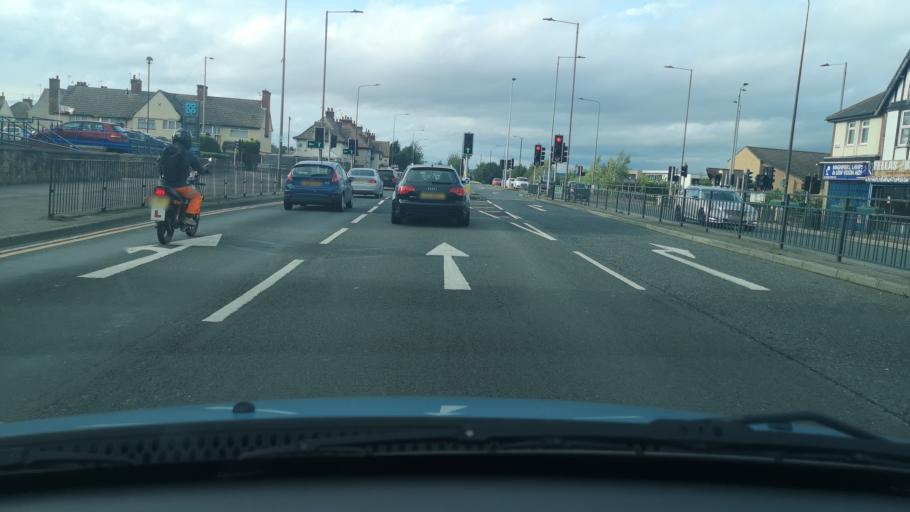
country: GB
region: England
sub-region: Doncaster
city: Carcroft
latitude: 53.5640
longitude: -1.1956
